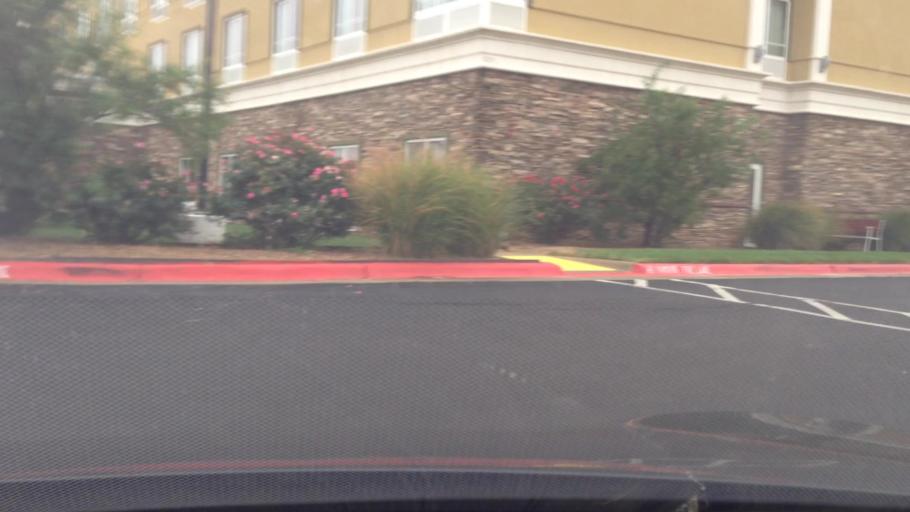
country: US
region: Texas
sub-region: Potter County
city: Amarillo
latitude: 35.1901
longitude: -101.9304
